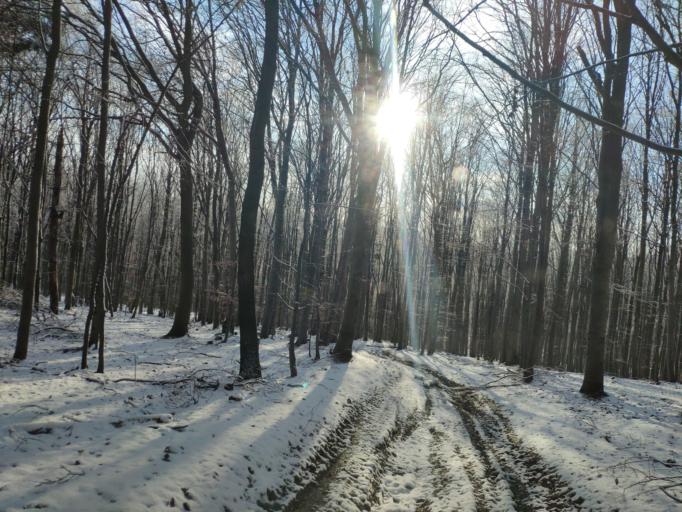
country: SK
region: Kosicky
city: Moldava nad Bodvou
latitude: 48.7429
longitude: 21.0874
